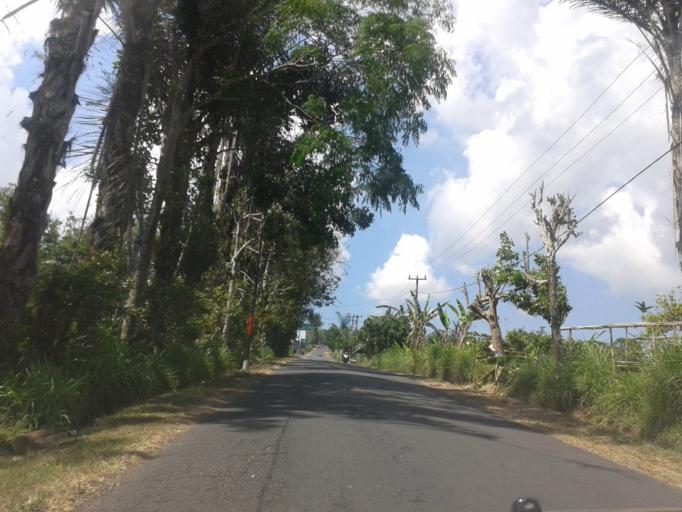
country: ID
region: Bali
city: Banjar Kedisan
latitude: -8.2957
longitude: 115.3394
